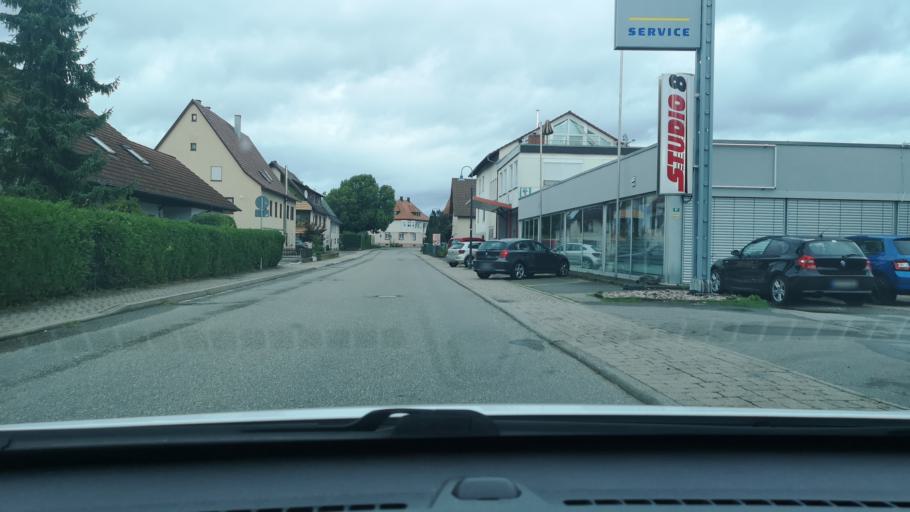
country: DE
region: Baden-Wuerttemberg
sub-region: Freiburg Region
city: Vohringen
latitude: 48.3374
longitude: 8.6617
